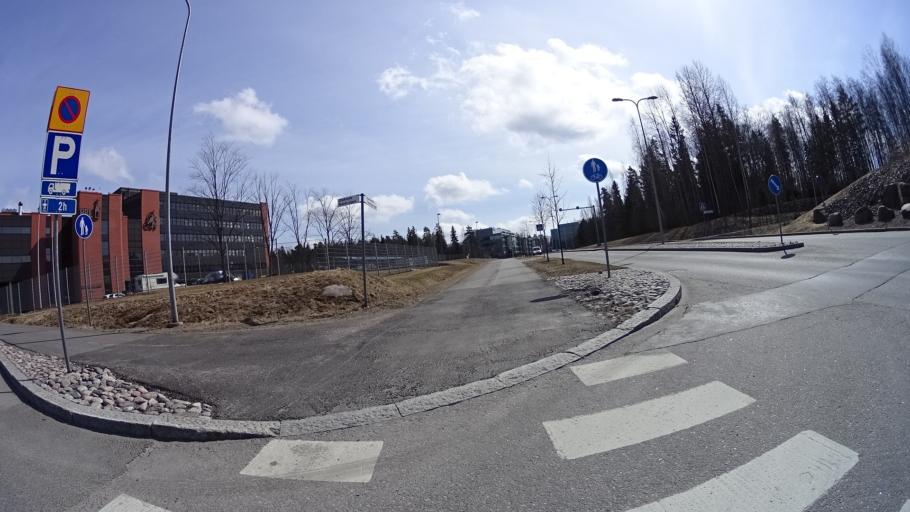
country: FI
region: Uusimaa
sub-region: Helsinki
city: Kilo
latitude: 60.2875
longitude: 24.8499
